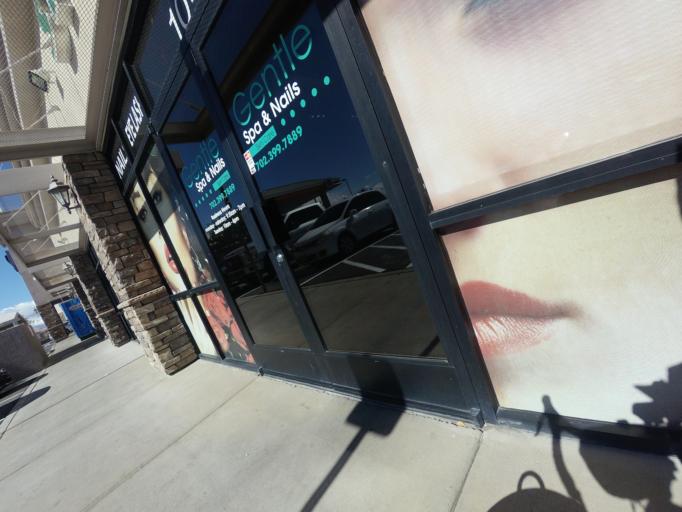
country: US
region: Nevada
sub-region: Clark County
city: Nellis Air Force Base
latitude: 36.2689
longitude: -115.1105
